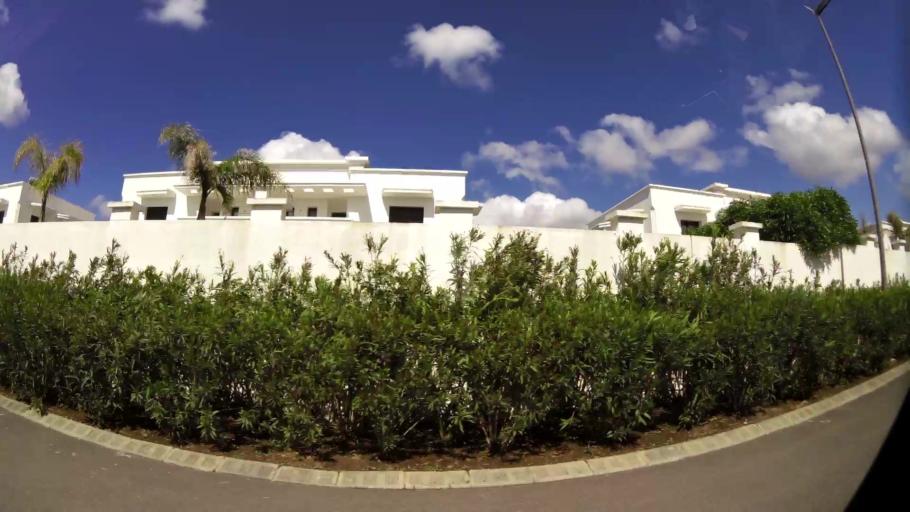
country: MA
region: Grand Casablanca
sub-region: Nouaceur
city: Bouskoura
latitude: 33.4684
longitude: -7.5965
